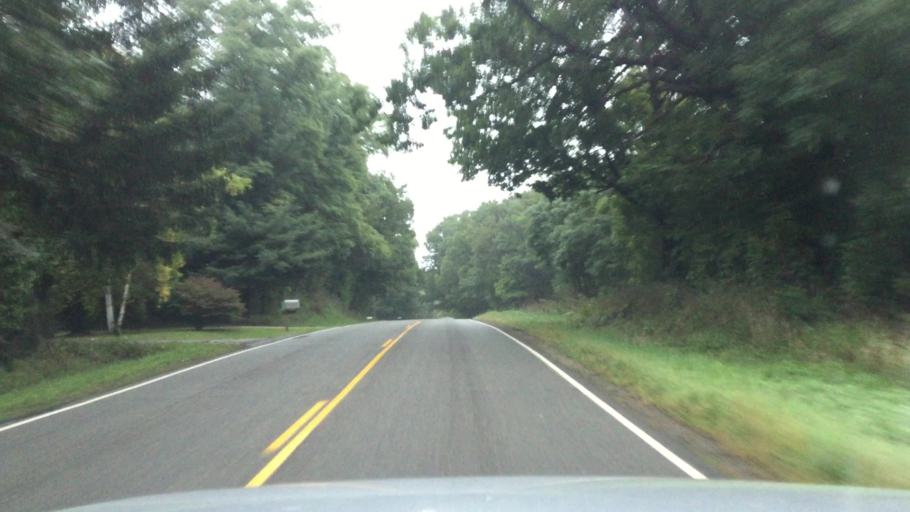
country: US
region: Michigan
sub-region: Shiawassee County
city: Corunna
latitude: 42.9311
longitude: -84.1243
